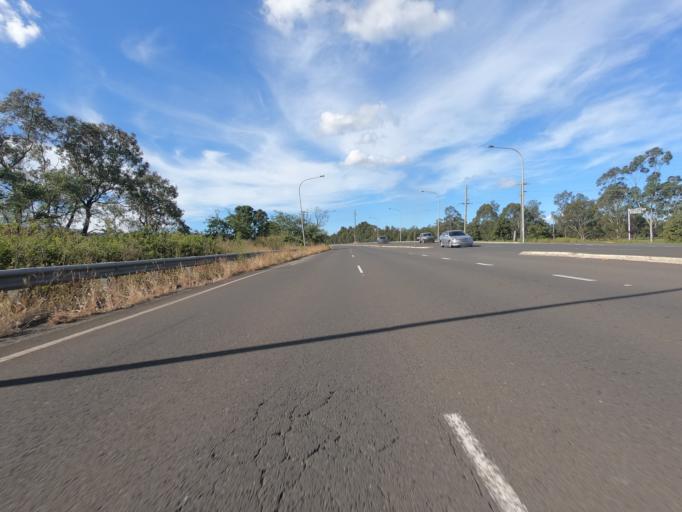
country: AU
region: New South Wales
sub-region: Wollongong
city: Koonawarra
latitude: -34.4745
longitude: 150.8119
